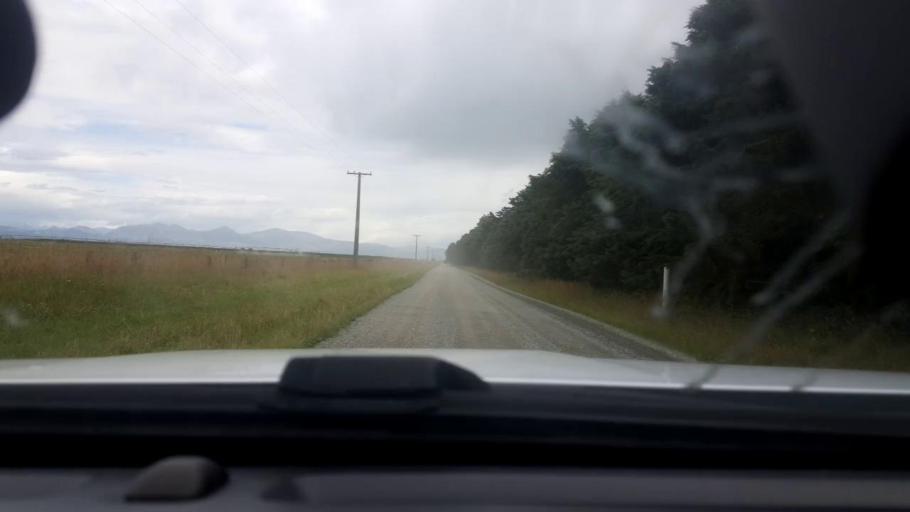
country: NZ
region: Canterbury
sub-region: Timaru District
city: Timaru
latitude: -44.1568
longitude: 171.4005
